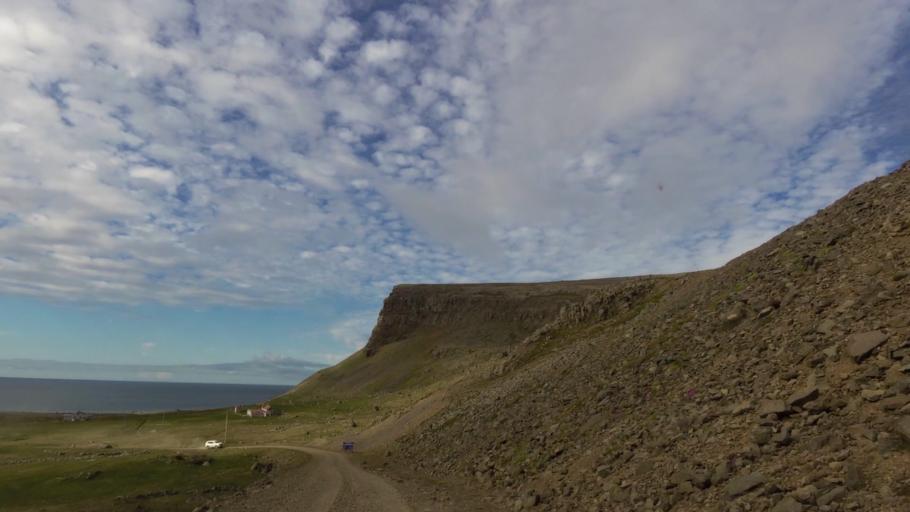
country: IS
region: West
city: Olafsvik
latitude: 65.6128
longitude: -24.3133
